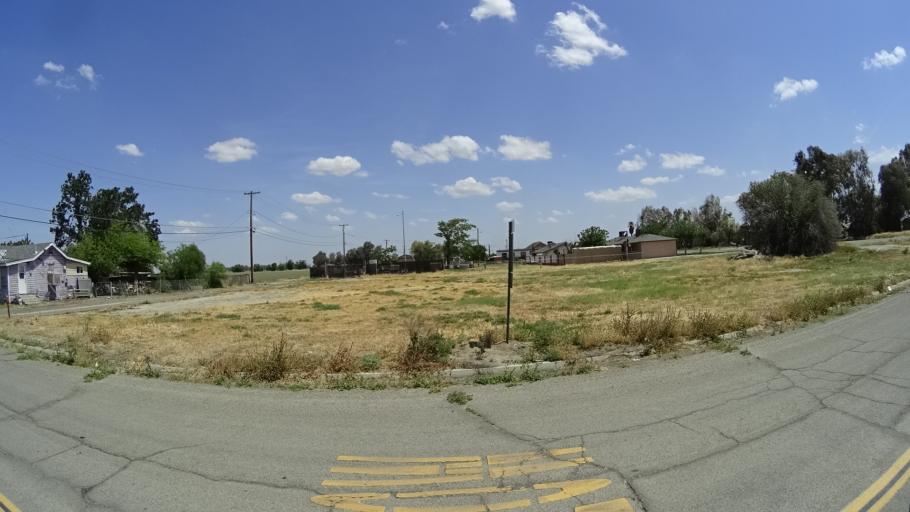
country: US
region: California
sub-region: Kings County
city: Stratford
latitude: 36.1899
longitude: -119.8207
